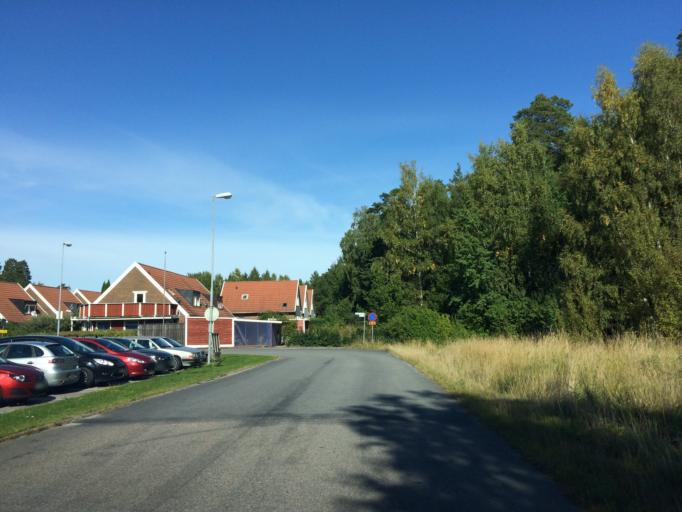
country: SE
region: Stockholm
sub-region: Sollentuna Kommun
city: Sollentuna
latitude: 59.4079
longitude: 17.9852
